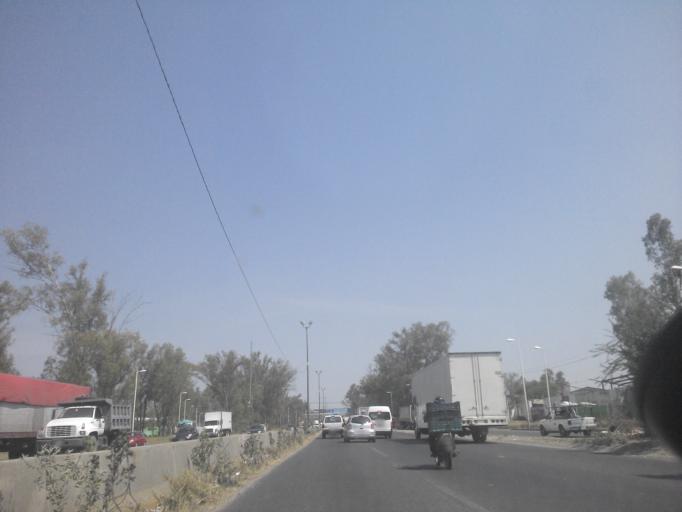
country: MX
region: Jalisco
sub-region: Tlajomulco de Zuniga
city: Palomar
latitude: 20.6396
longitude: -103.4397
